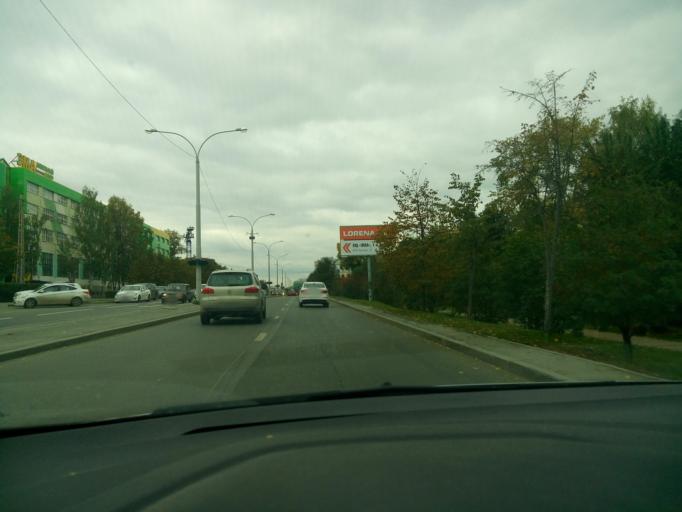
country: RU
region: Sverdlovsk
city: Yekaterinburg
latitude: 56.8382
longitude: 60.5764
